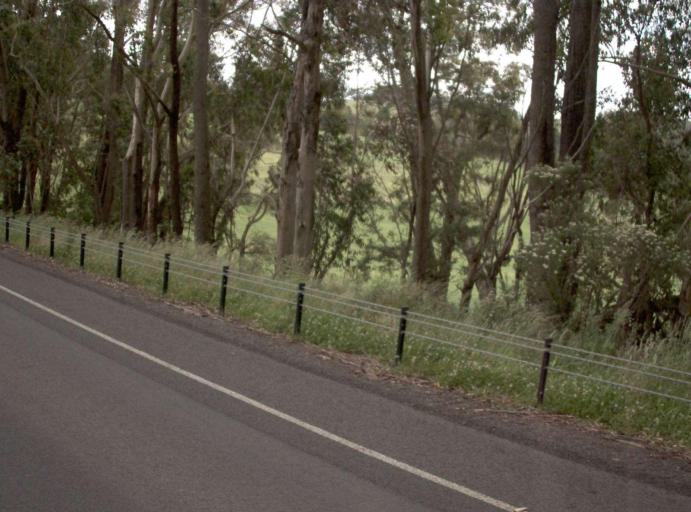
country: AU
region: Victoria
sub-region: Baw Baw
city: Warragul
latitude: -38.0743
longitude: 145.9652
